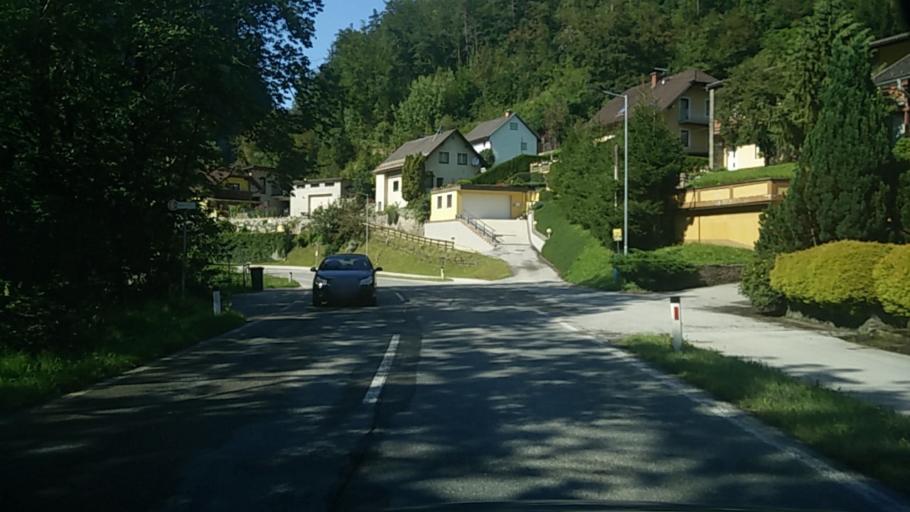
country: AT
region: Carinthia
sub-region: Politischer Bezirk Volkermarkt
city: Bad Eisenkappel
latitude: 46.4935
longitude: 14.5846
